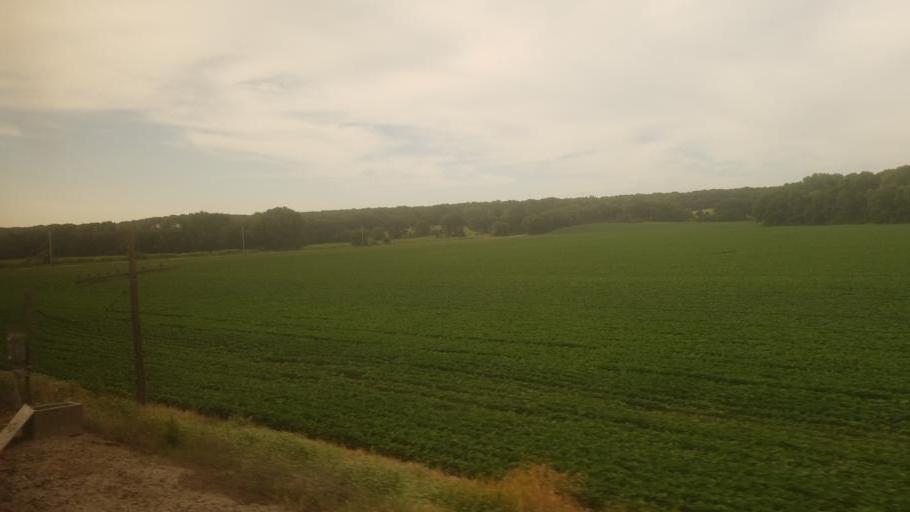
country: US
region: Kansas
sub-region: Shawnee County
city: Topeka
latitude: 39.0577
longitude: -95.5317
